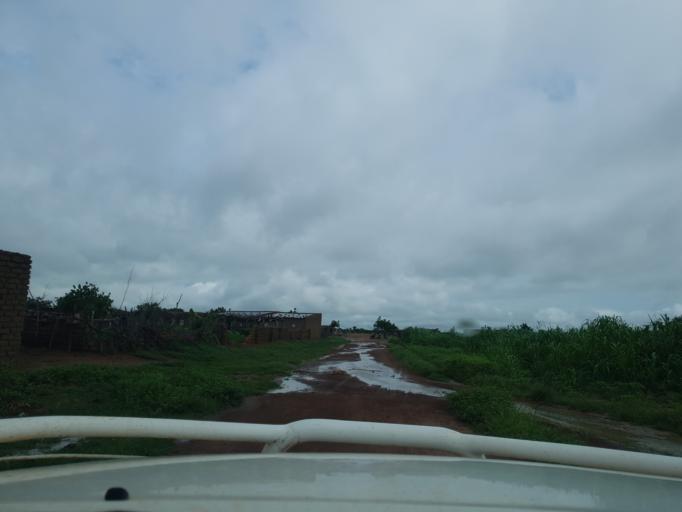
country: ML
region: Segou
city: Bla
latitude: 12.8048
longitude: -5.6057
